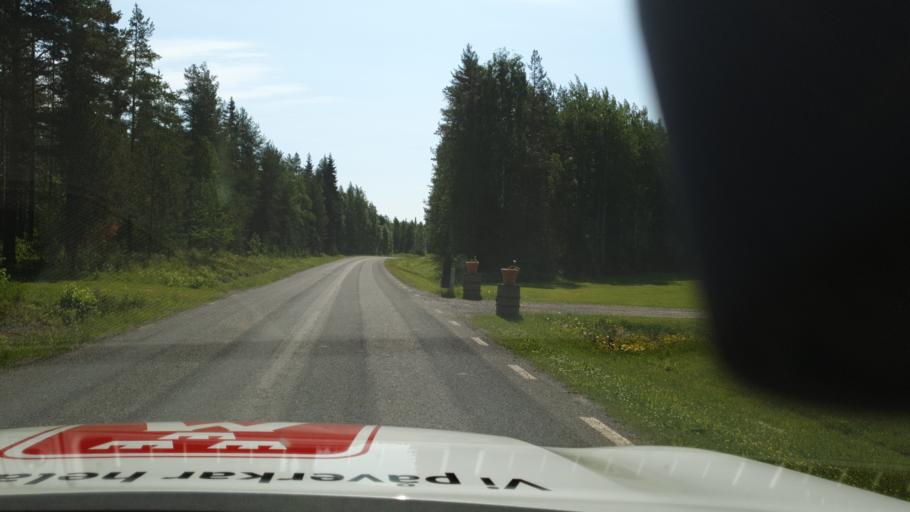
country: SE
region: Vaesterbotten
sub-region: Skelleftea Kommun
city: Langsele
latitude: 65.0222
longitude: 20.0731
